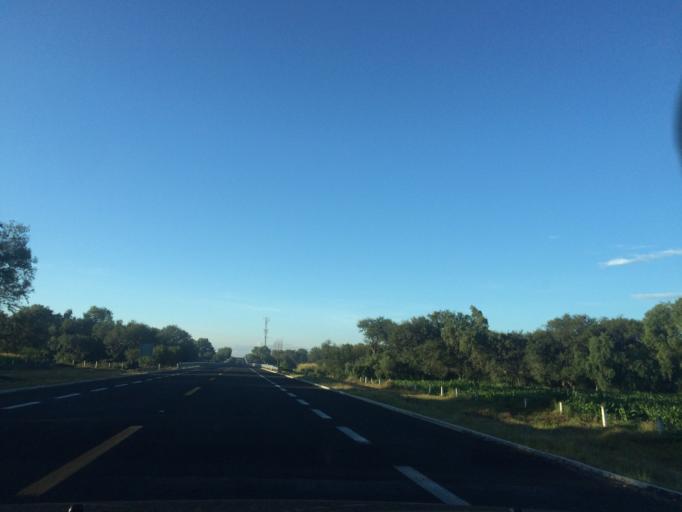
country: MX
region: Puebla
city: Santiago Miahuatlan
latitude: 18.5392
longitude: -97.4597
